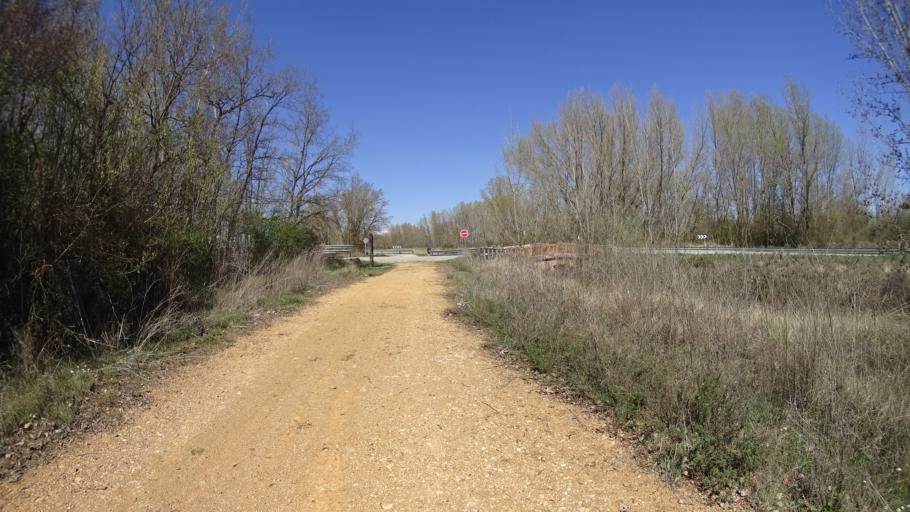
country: ES
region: Castille and Leon
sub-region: Provincia de Burgos
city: Rezmondo
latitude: 42.5110
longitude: -4.2726
